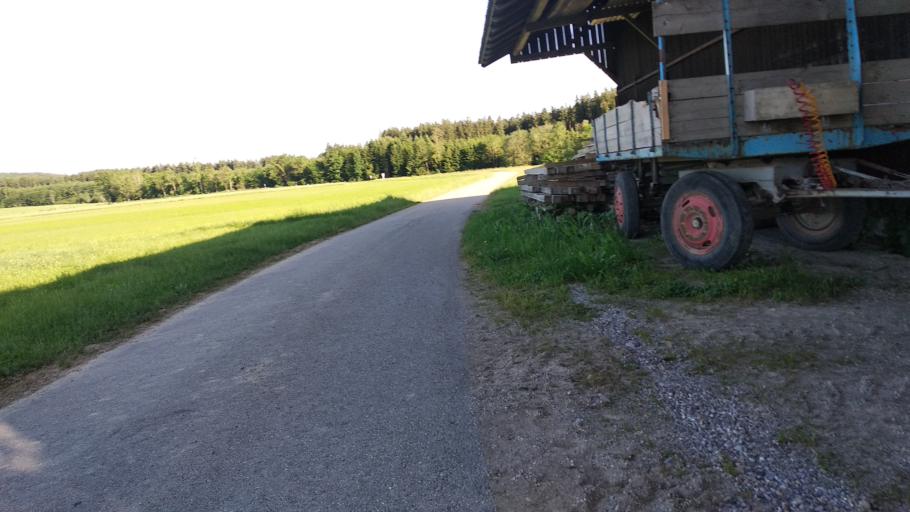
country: DE
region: Bavaria
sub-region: Swabia
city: Kronburg
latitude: 47.9048
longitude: 10.1416
